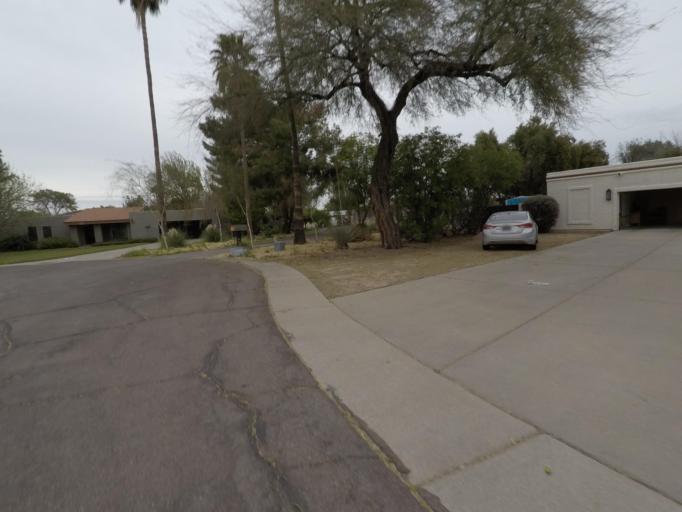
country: US
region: Arizona
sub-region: Maricopa County
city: Guadalupe
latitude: 33.3404
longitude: -111.9256
